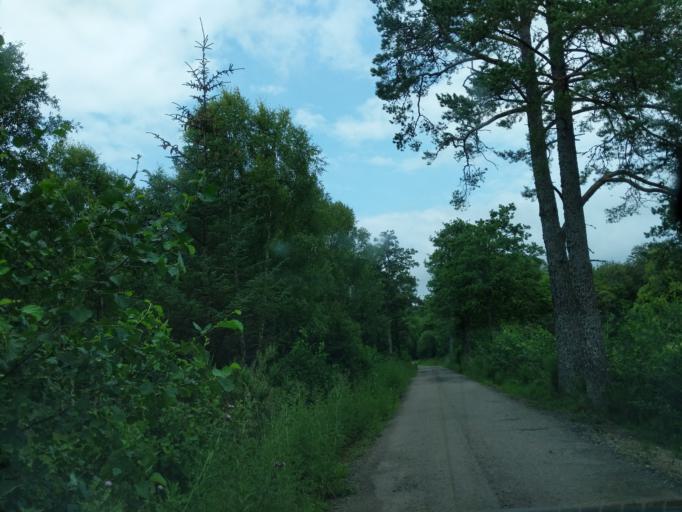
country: GB
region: Scotland
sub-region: Moray
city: Rothes
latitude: 57.4759
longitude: -3.2377
